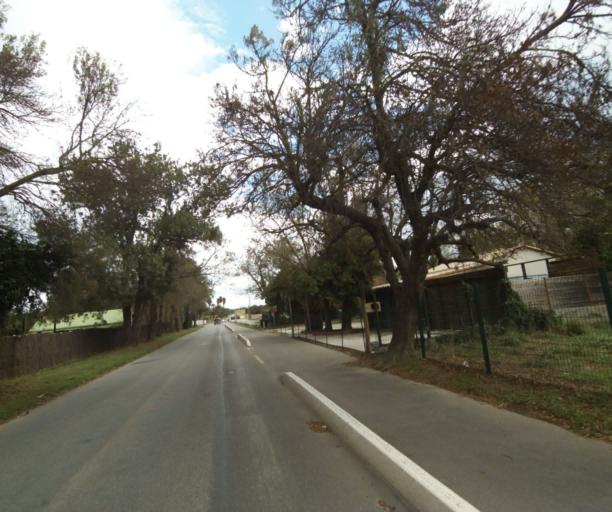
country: FR
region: Languedoc-Roussillon
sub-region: Departement des Pyrenees-Orientales
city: Argelers
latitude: 42.5638
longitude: 3.0351
